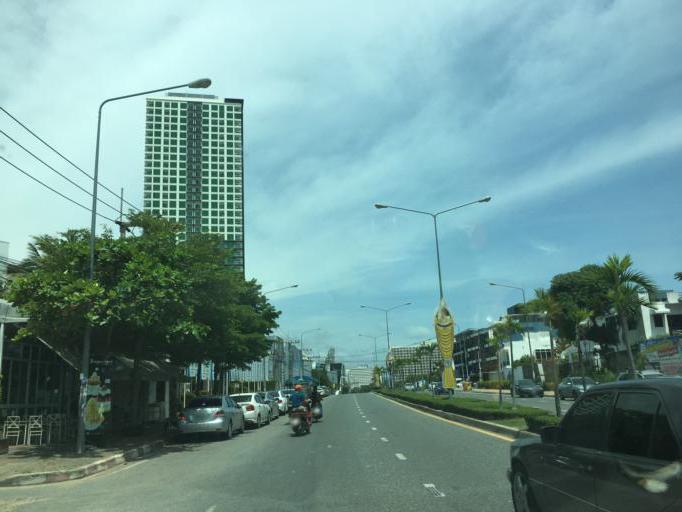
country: TH
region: Chon Buri
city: Phatthaya
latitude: 12.8951
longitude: 100.8758
